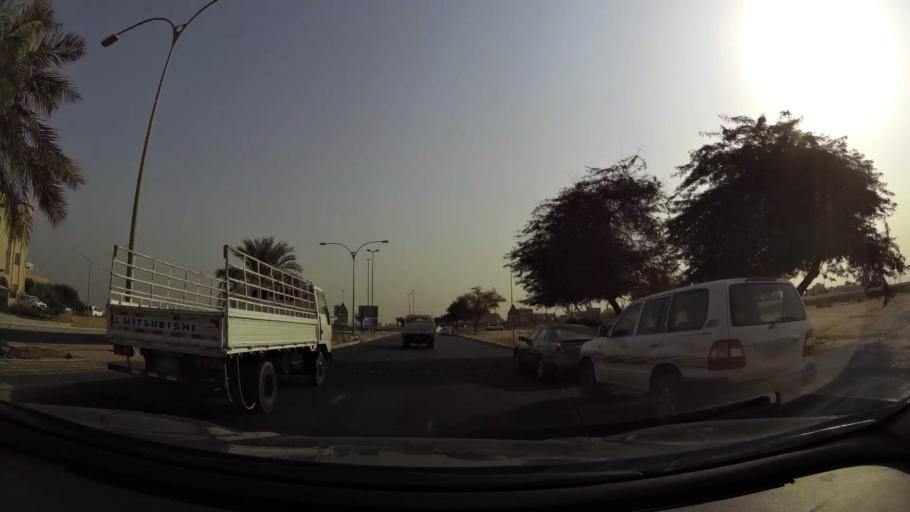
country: KW
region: Al Ahmadi
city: Ar Riqqah
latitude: 29.1226
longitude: 48.1047
